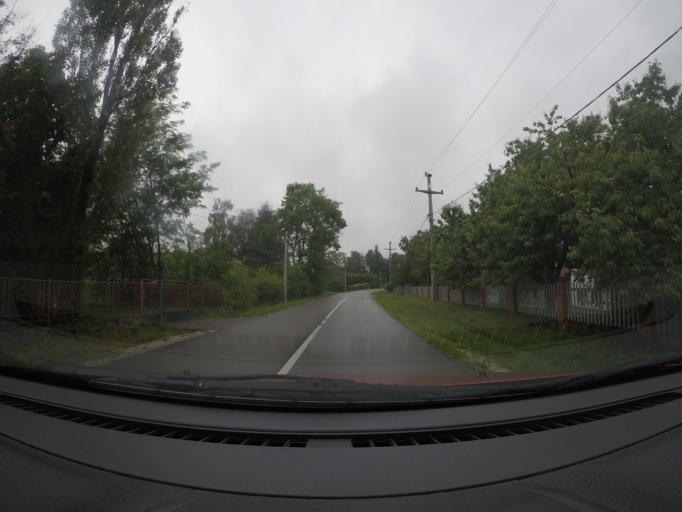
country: RS
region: Central Serbia
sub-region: Belgrade
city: Sopot
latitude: 44.5470
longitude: 20.5383
